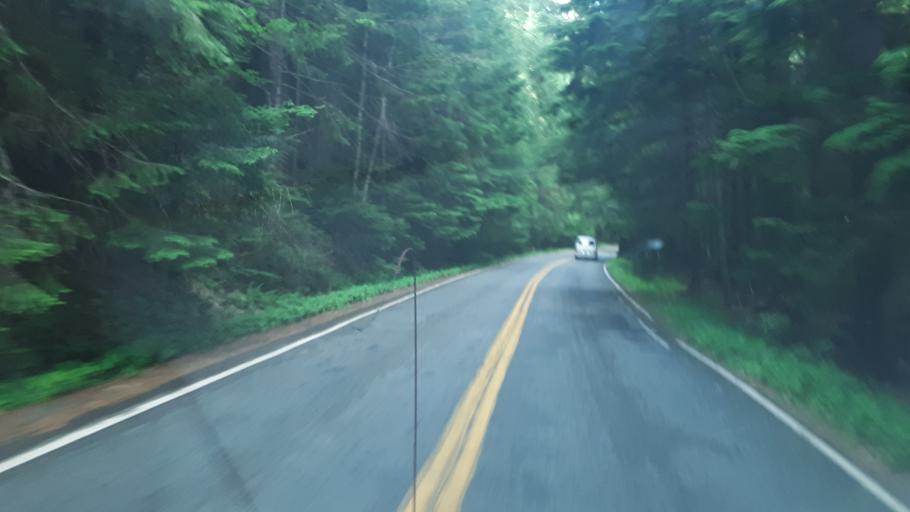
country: US
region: Washington
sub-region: Pierce County
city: Buckley
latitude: 46.7717
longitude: -121.5486
